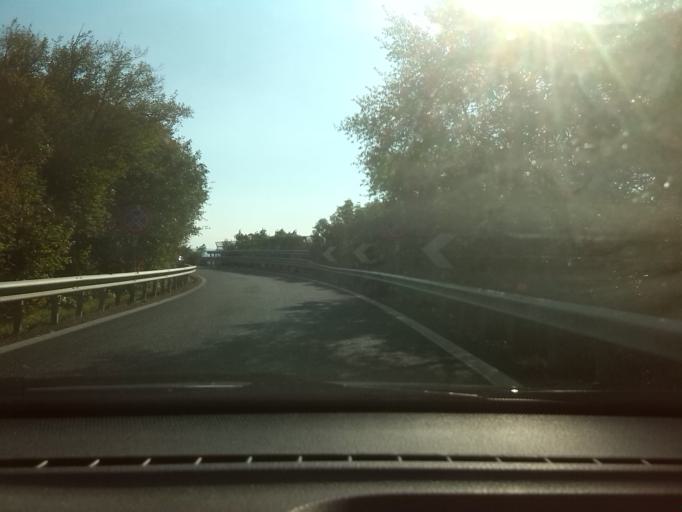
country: IT
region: Friuli Venezia Giulia
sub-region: Provincia di Trieste
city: Sistiana-Visogliano
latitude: 45.7625
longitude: 13.6402
